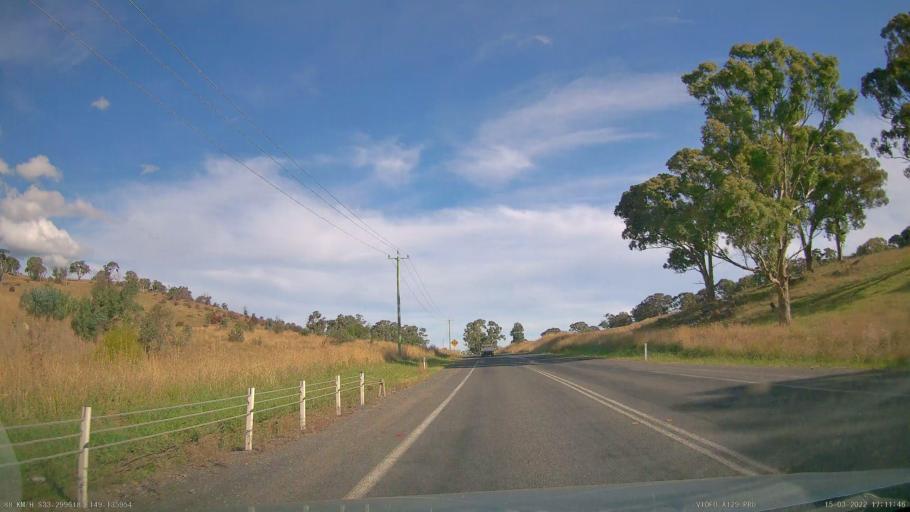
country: AU
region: New South Wales
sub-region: Orange Municipality
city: Orange
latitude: -33.2997
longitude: 149.1359
